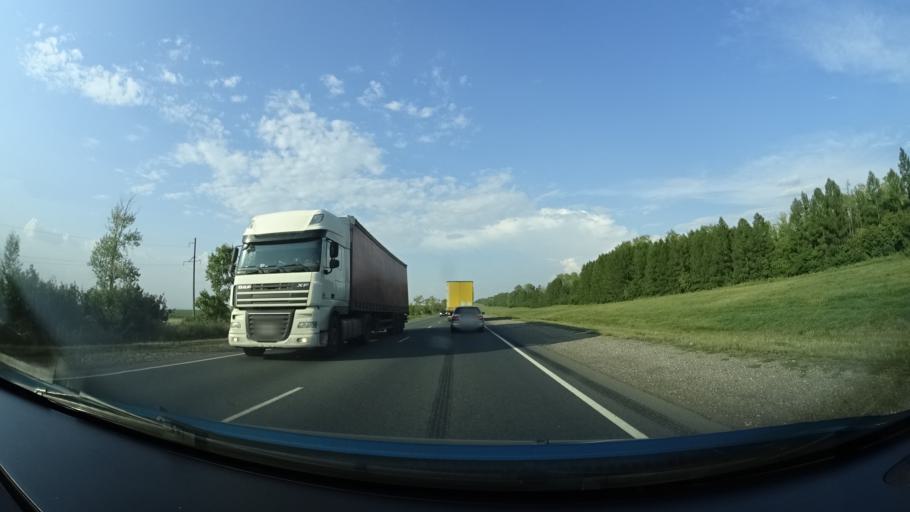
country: RU
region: Samara
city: Krasnyy Yar
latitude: 53.6544
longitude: 50.7466
